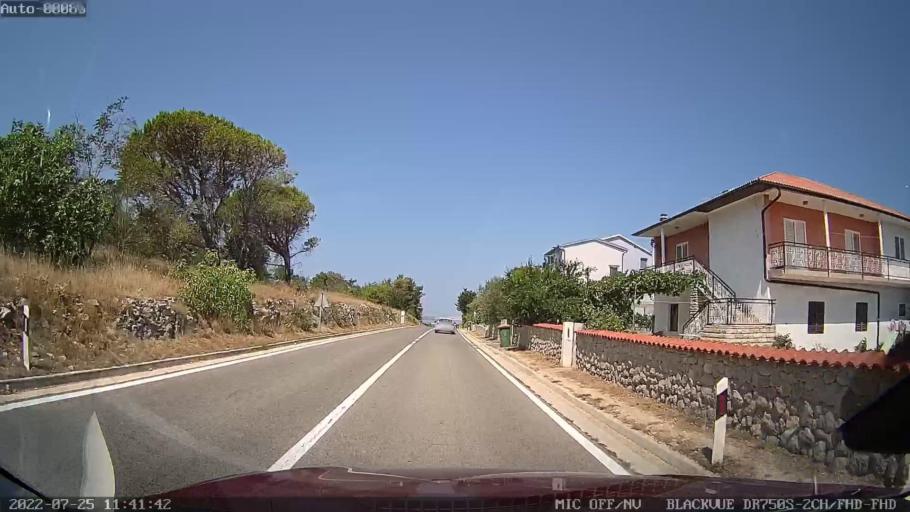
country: HR
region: Zadarska
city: Razanac
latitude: 44.2697
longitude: 15.3443
